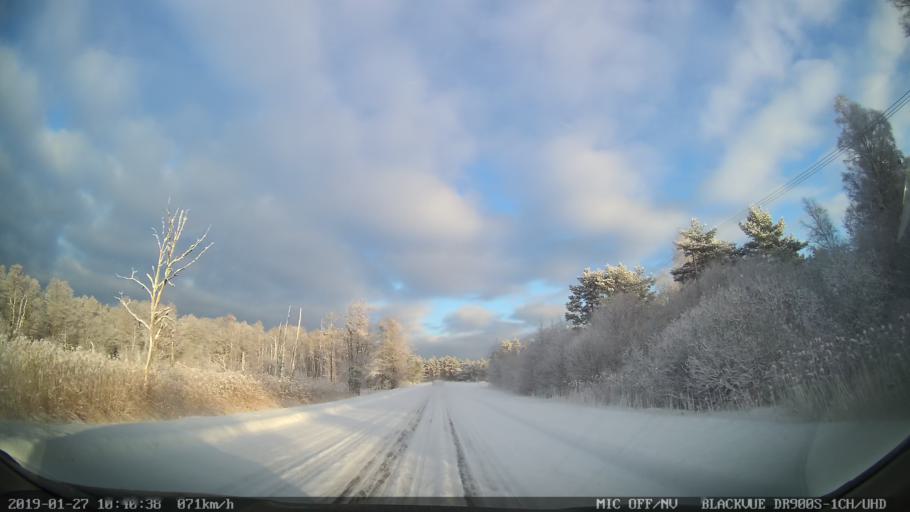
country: EE
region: Harju
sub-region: Raasiku vald
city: Raasiku
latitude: 59.5045
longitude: 25.2622
